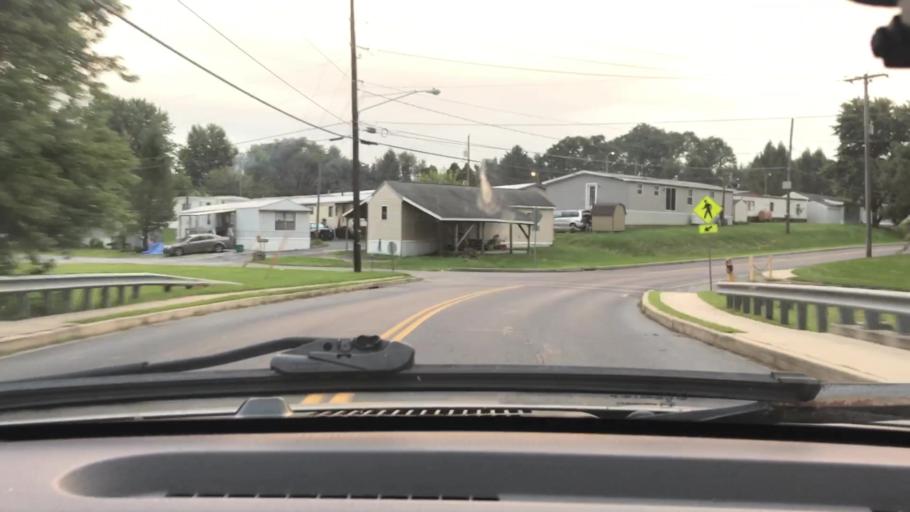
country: US
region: Pennsylvania
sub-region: Lancaster County
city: Elizabethtown
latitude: 40.1643
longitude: -76.5915
